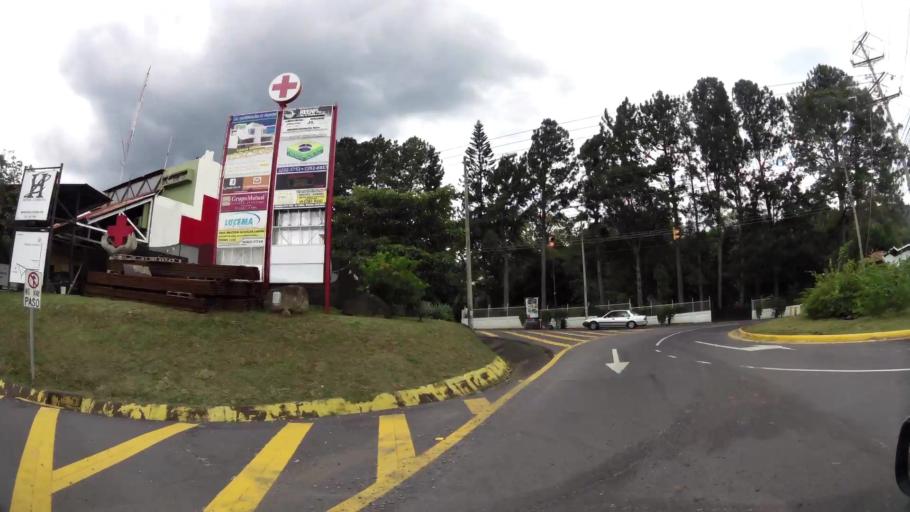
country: CR
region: San Jose
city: Santa Ana
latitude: 9.9338
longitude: -84.1887
